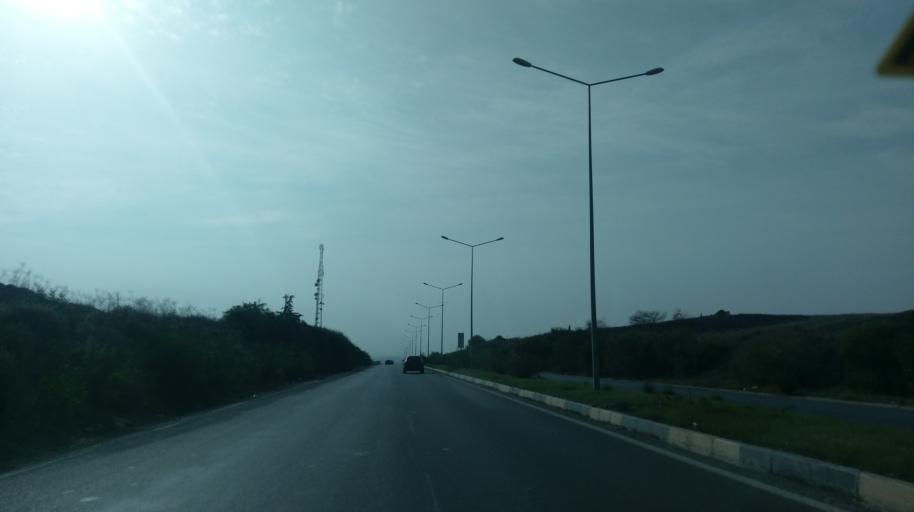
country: CY
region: Lefkosia
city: Nicosia
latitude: 35.2343
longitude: 33.3117
